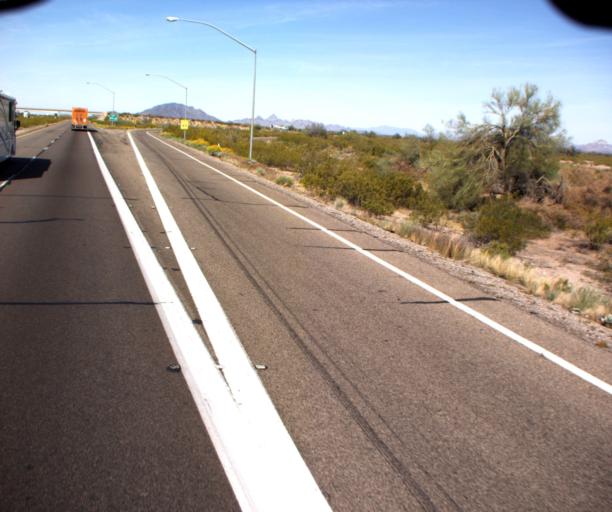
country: US
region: Arizona
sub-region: Maricopa County
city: Buckeye
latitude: 33.4964
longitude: -112.9316
